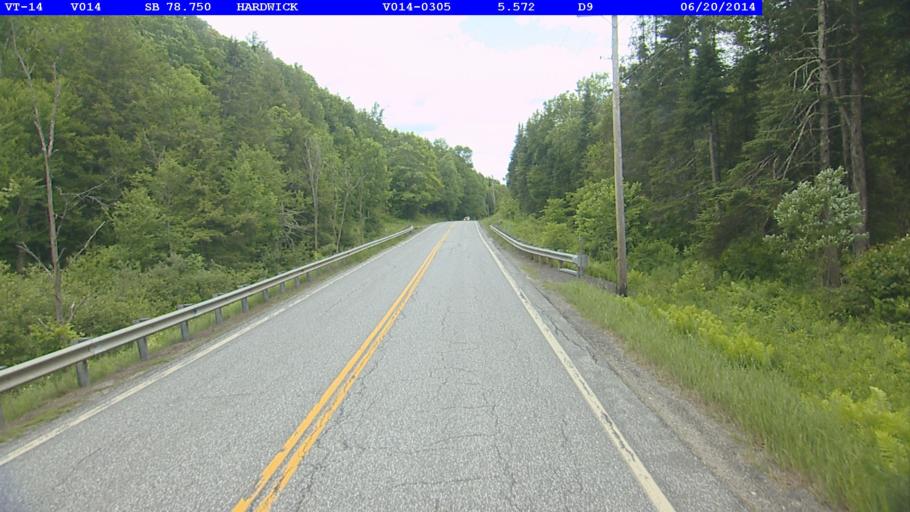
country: US
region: Vermont
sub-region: Caledonia County
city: Hardwick
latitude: 44.5735
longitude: -72.3651
